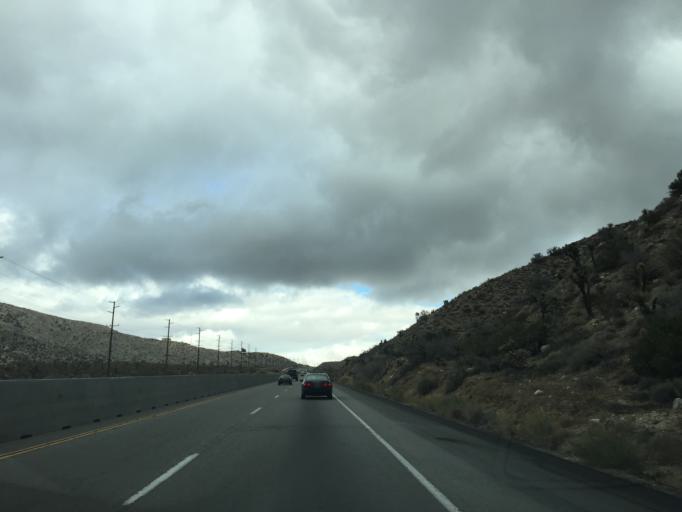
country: US
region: California
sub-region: San Bernardino County
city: Yucca Valley
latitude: 34.1040
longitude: -116.4917
